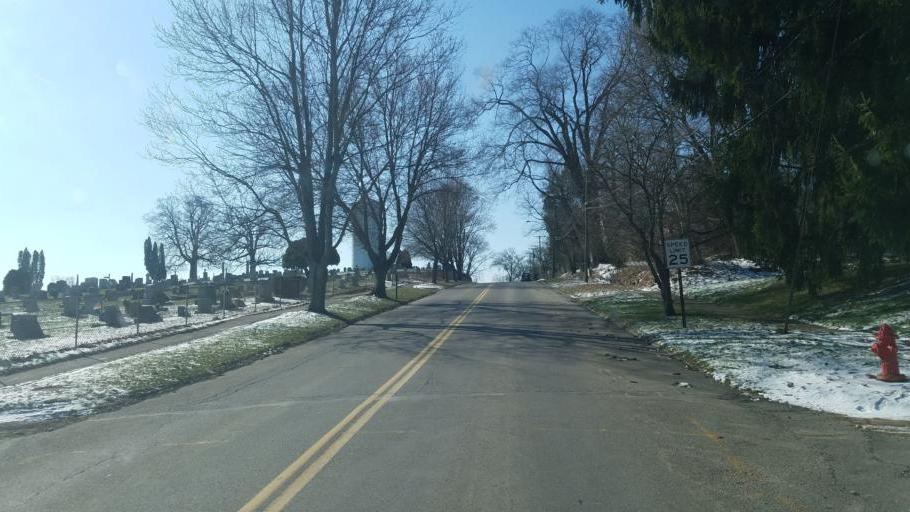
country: US
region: Ohio
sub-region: Knox County
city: Mount Vernon
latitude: 40.4055
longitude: -82.4868
